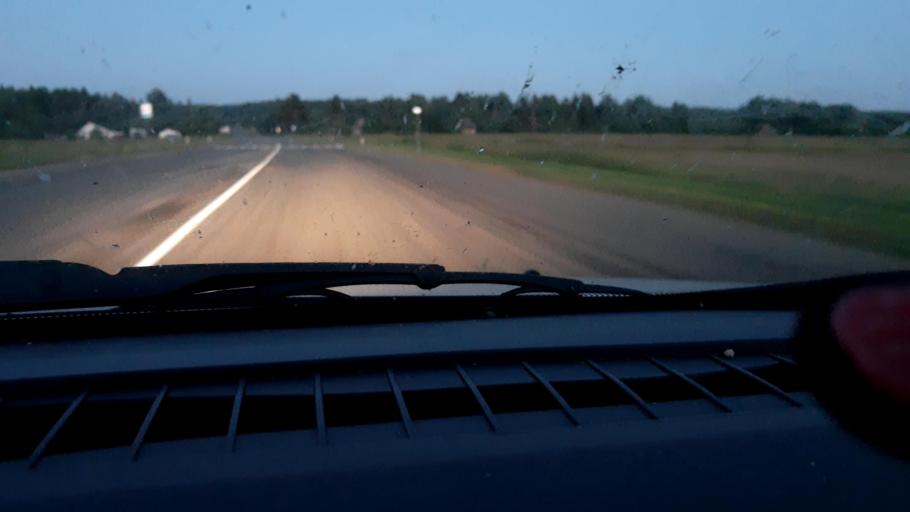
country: RU
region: Nizjnij Novgorod
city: Tonkino
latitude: 57.3544
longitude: 46.4313
